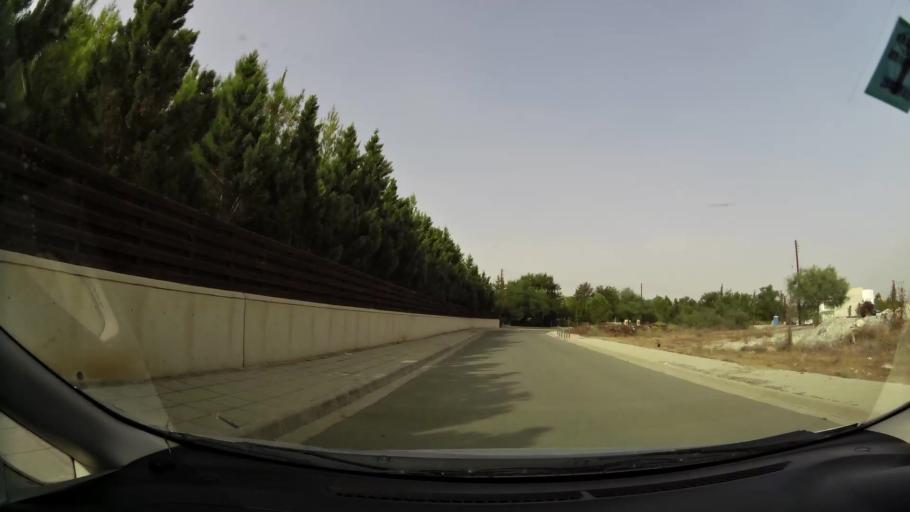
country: CY
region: Lefkosia
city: Geri
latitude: 35.0786
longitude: 33.3886
